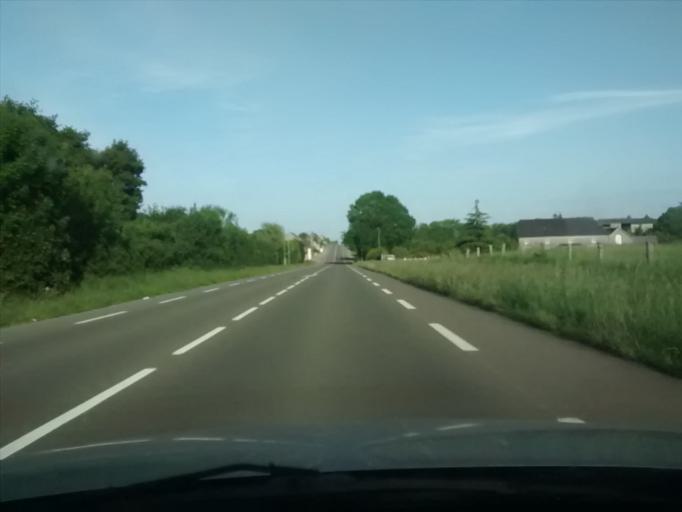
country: FR
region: Pays de la Loire
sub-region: Departement de la Mayenne
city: Soulge-sur-Ouette
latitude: 48.0565
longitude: -0.5589
